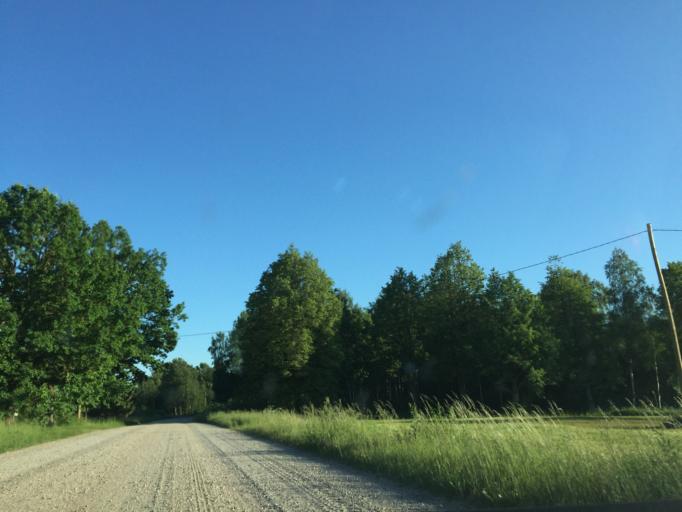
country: LV
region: Broceni
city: Broceni
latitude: 56.8619
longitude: 22.5792
